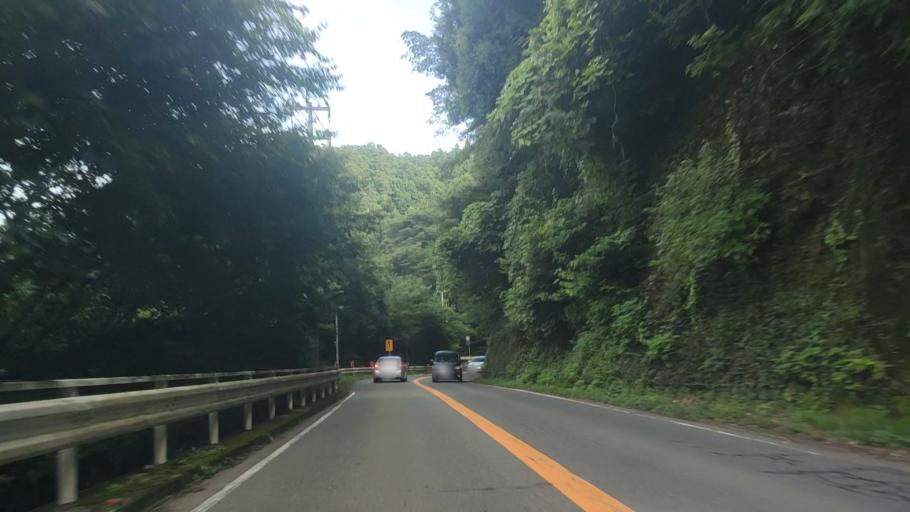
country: JP
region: Gunma
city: Omamacho-omama
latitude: 36.4549
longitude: 139.2658
